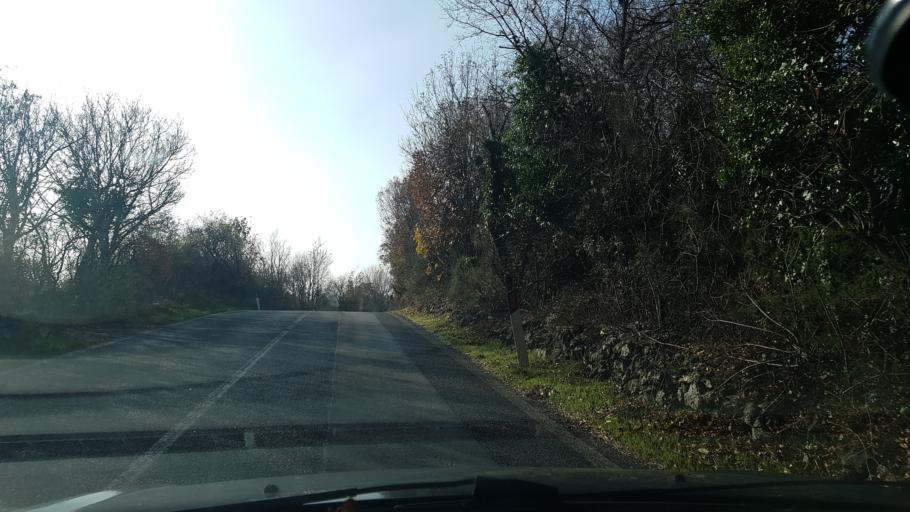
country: IT
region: Friuli Venezia Giulia
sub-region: Provincia di Gorizia
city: Doberdo del Lago
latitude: 45.8391
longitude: 13.5285
